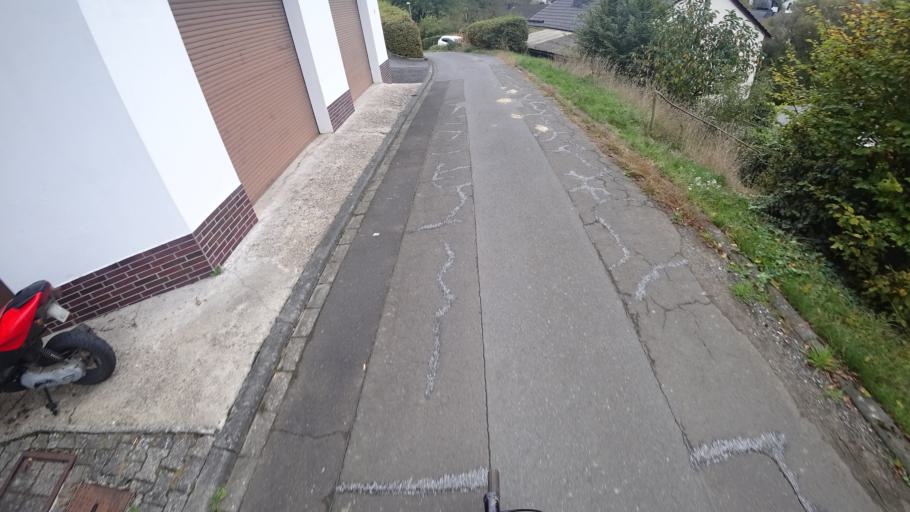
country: DE
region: Rheinland-Pfalz
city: Isselbach
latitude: 50.3905
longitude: 7.8921
